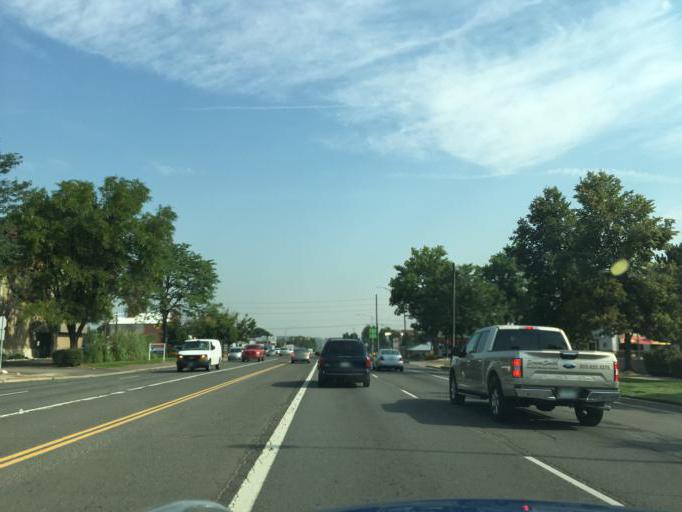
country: US
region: Colorado
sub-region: Jefferson County
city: Wheat Ridge
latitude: 39.7717
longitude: -105.0814
